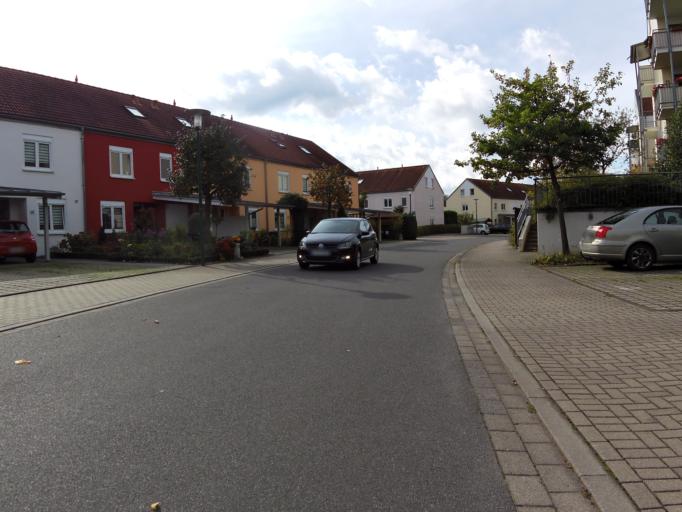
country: DE
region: Saxony
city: Grossposna
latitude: 51.3019
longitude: 12.4405
